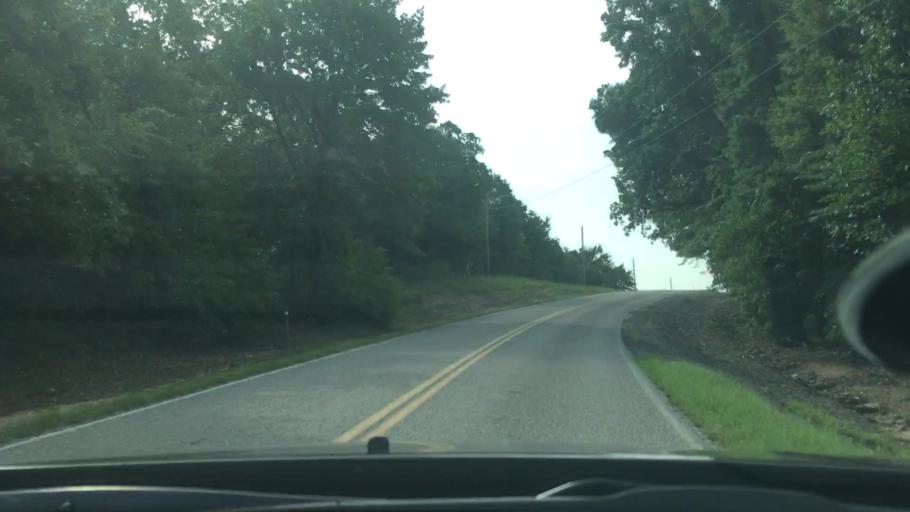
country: US
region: Oklahoma
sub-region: Johnston County
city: Tishomingo
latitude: 34.2076
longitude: -96.5823
